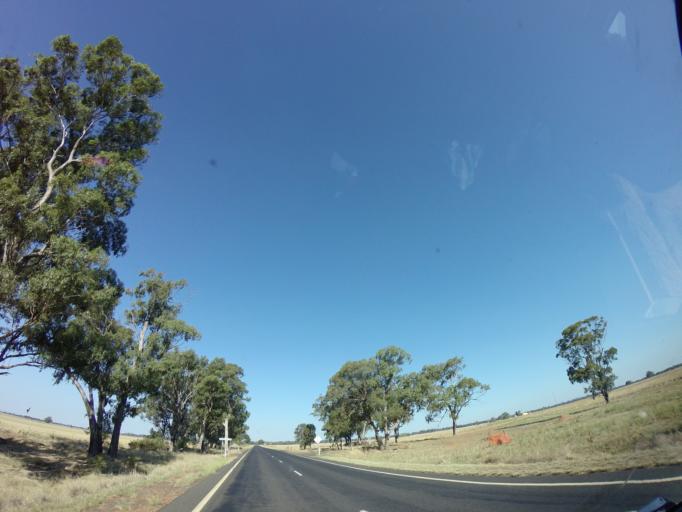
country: AU
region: New South Wales
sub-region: Gilgandra
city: Gilgandra
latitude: -31.7055
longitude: 148.6144
